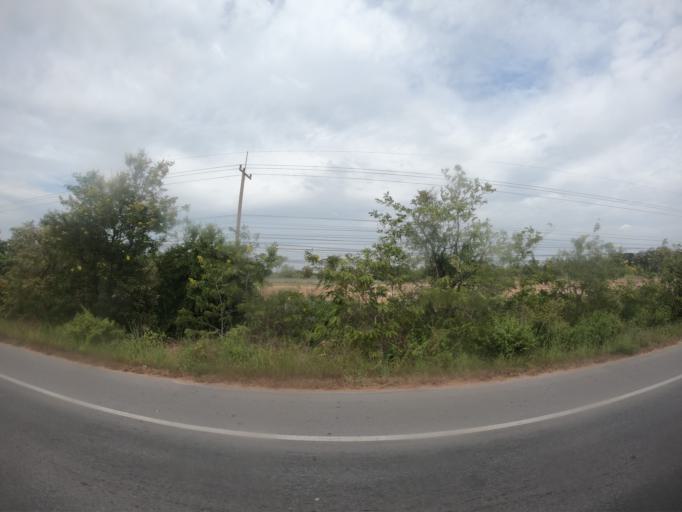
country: TH
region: Roi Et
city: Changhan
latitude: 16.0779
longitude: 103.5831
